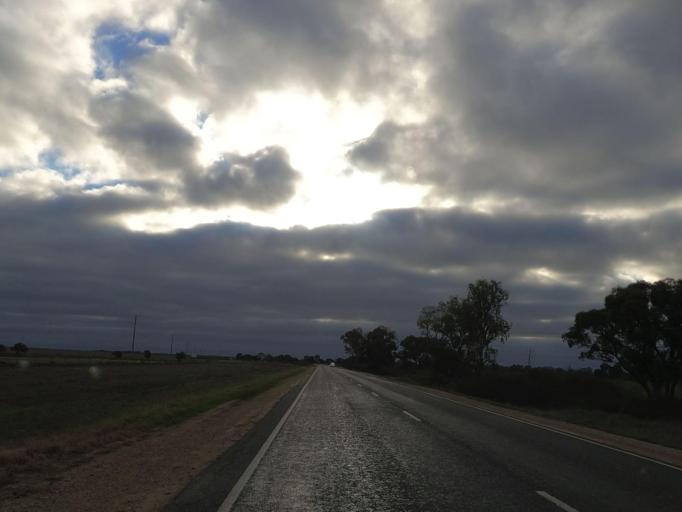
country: AU
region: Victoria
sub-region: Swan Hill
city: Swan Hill
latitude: -35.6543
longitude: 143.8486
